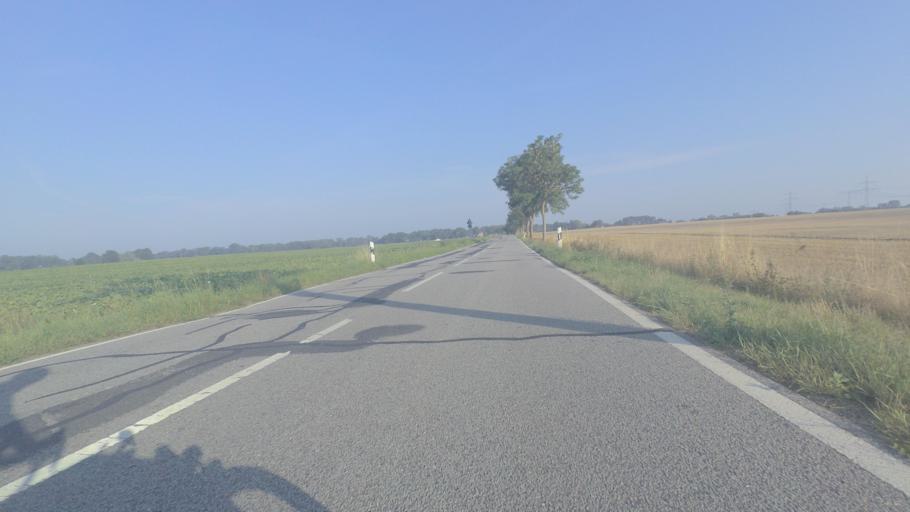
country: DE
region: Mecklenburg-Vorpommern
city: Demmin
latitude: 53.9482
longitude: 13.1195
